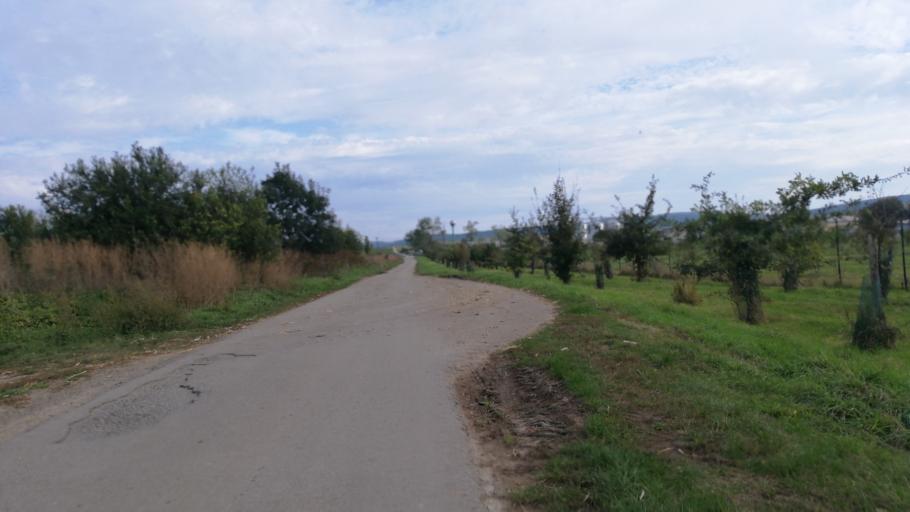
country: CZ
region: South Moravian
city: Sudomerice
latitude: 48.8508
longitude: 17.2473
